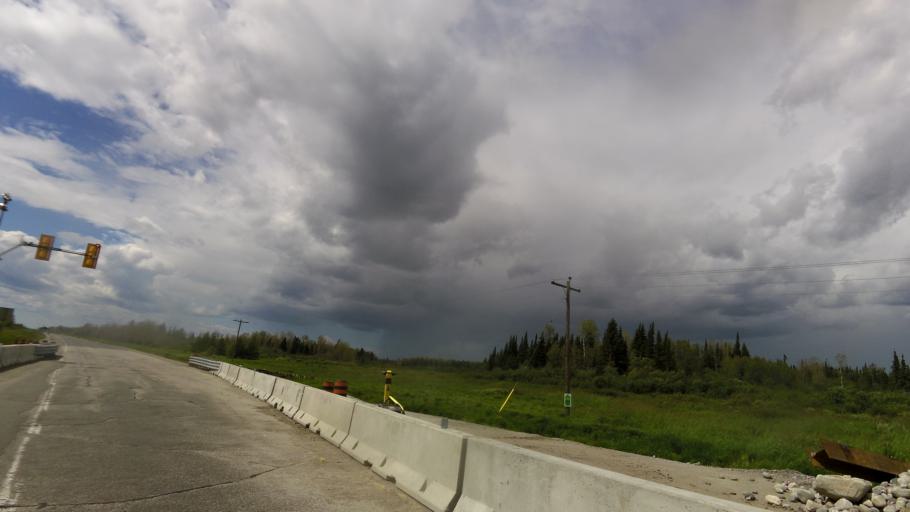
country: CA
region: Ontario
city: Hearst
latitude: 49.5936
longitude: -83.1713
